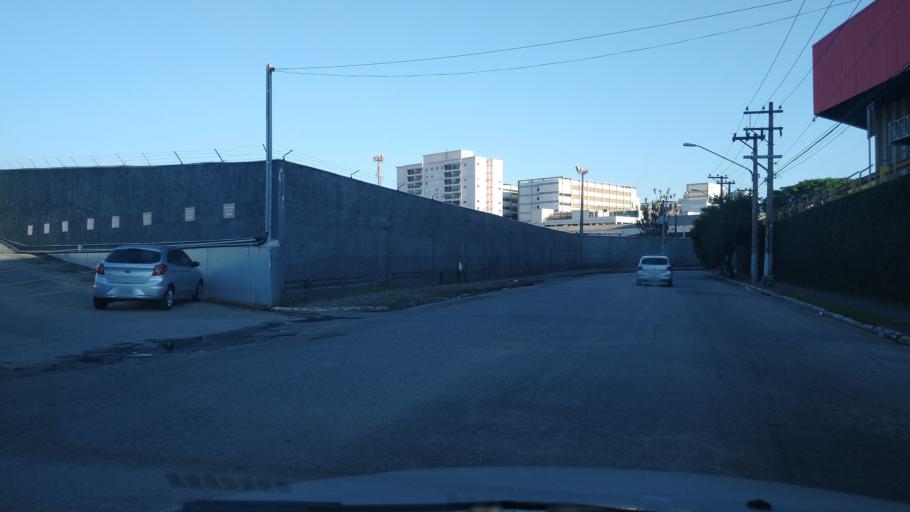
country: BR
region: Sao Paulo
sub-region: Sao Paulo
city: Sao Paulo
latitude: -23.5100
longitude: -46.6100
